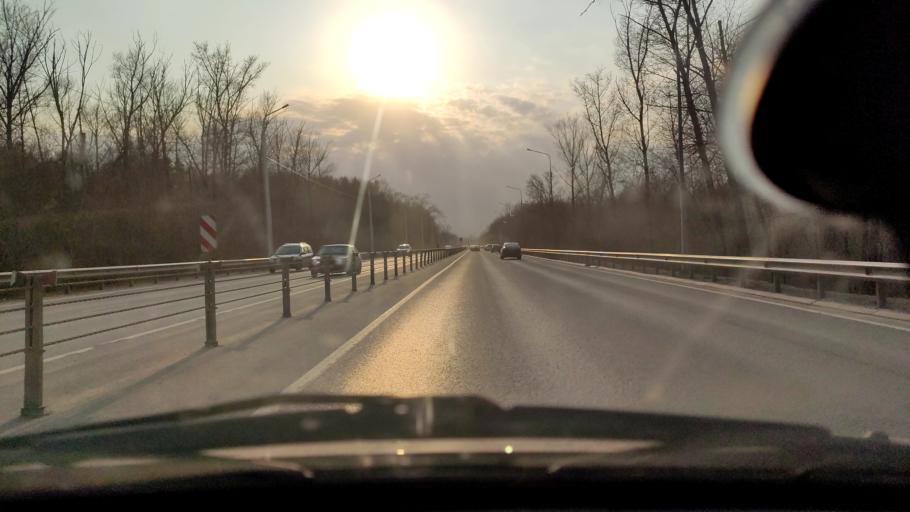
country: RU
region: Bashkortostan
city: Ufa
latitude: 54.6997
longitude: 55.9349
